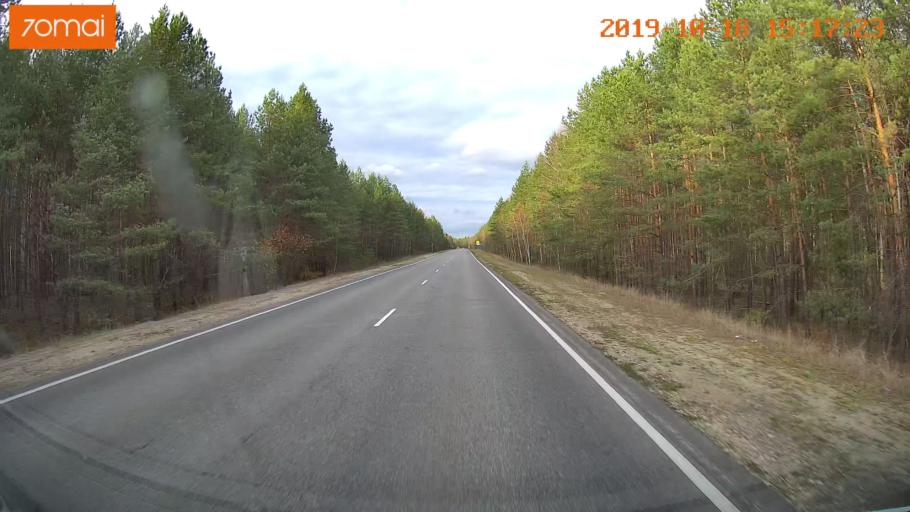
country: RU
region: Vladimir
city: Anopino
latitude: 55.6490
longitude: 40.7264
